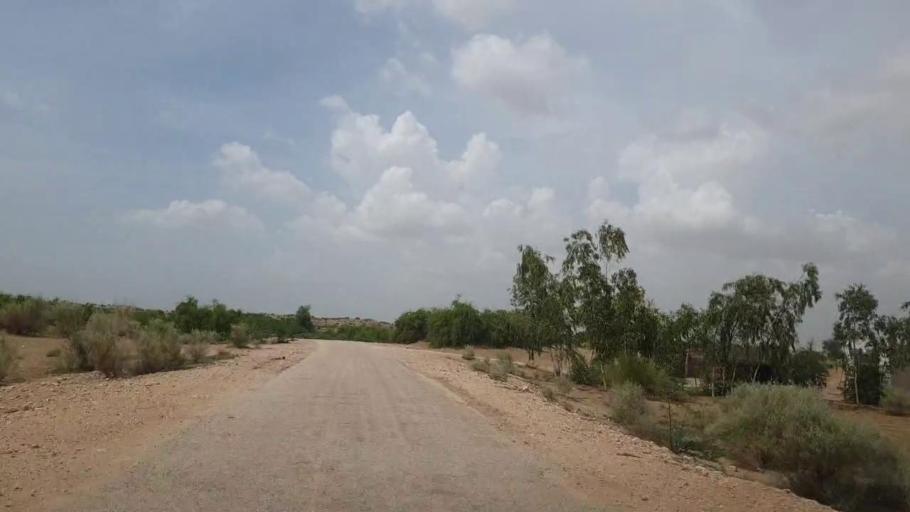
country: PK
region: Sindh
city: Kot Diji
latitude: 27.2454
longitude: 69.0782
